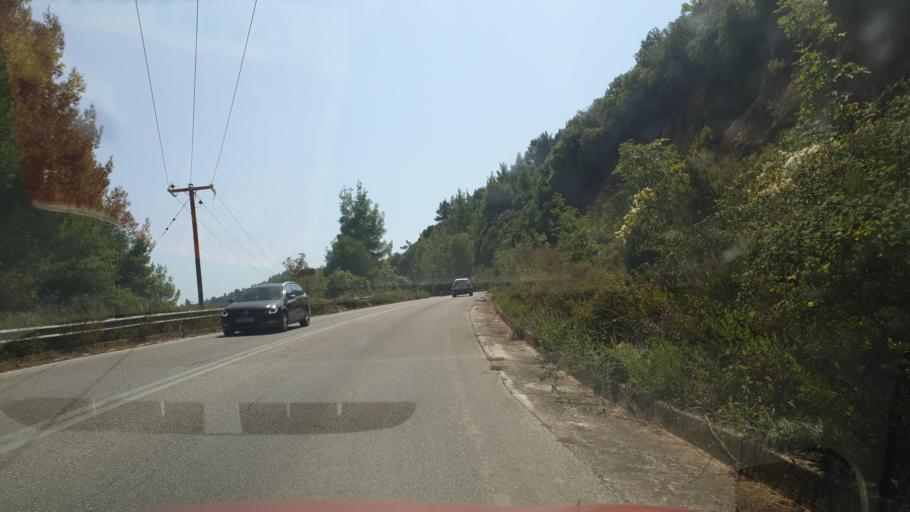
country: GR
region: Central Macedonia
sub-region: Nomos Chalkidikis
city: Neos Marmaras
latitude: 40.1681
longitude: 23.8619
